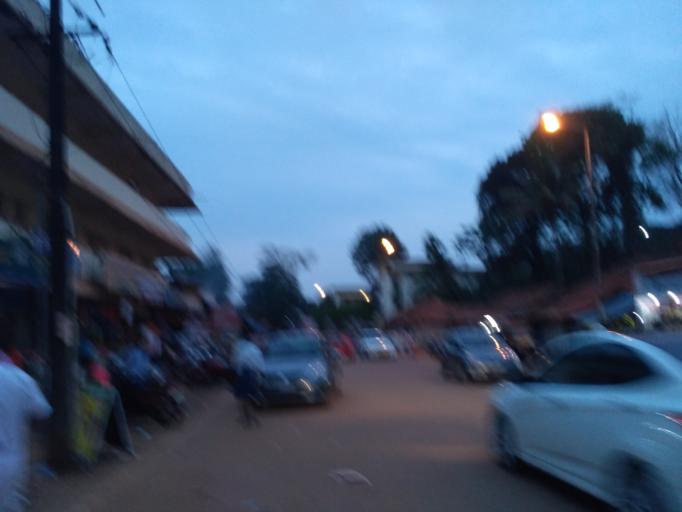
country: IN
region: Karnataka
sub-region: Dakshina Kannada
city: Sulya
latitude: 12.6640
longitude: 75.6137
